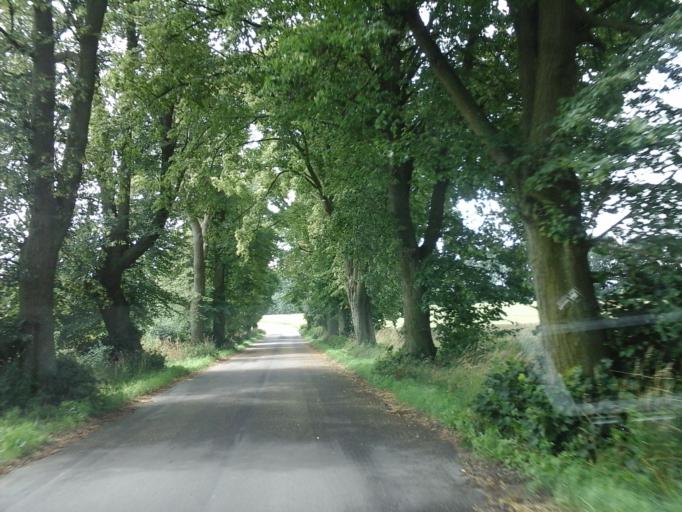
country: PL
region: West Pomeranian Voivodeship
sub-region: Powiat choszczenski
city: Krzecin
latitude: 53.0475
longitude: 15.4627
